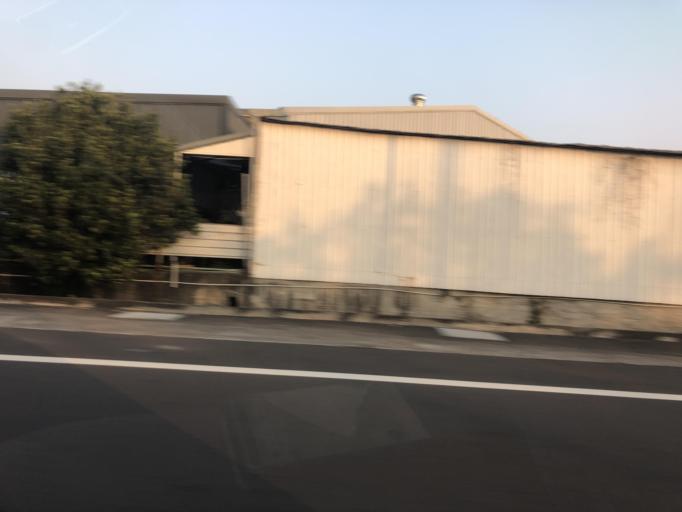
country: TW
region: Taiwan
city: Xinying
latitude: 23.2028
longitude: 120.2701
